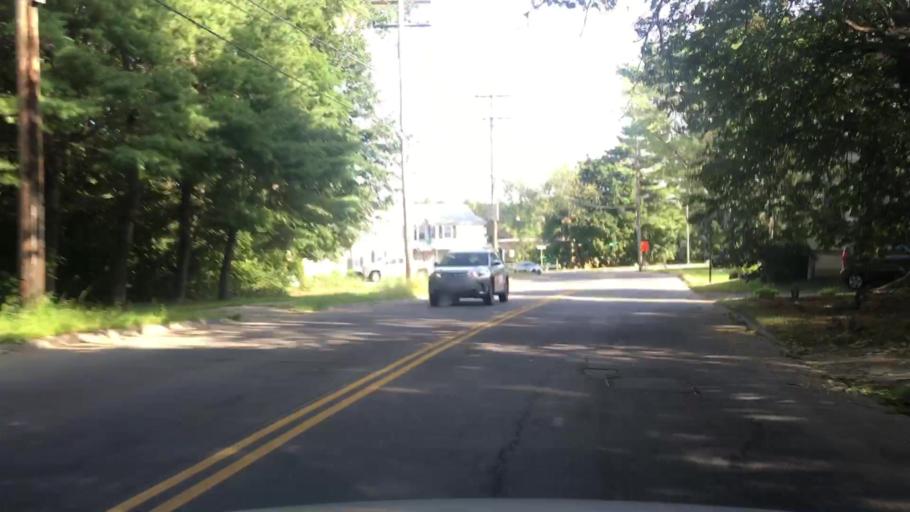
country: US
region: Maine
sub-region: Kennebec County
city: Waterville
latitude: 44.5492
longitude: -69.6436
